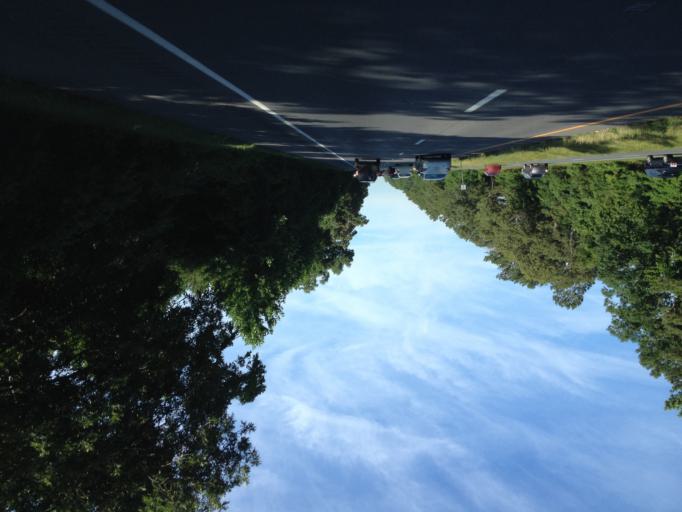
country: US
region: Delaware
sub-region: Sussex County
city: Millsboro
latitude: 38.6039
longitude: -75.3217
